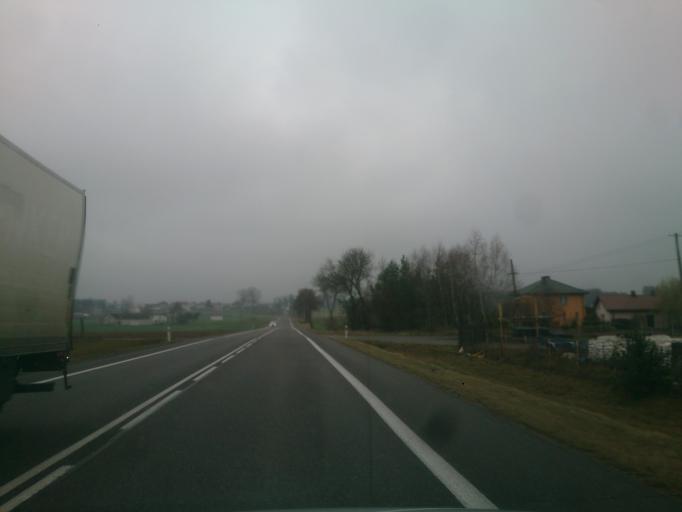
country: PL
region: Masovian Voivodeship
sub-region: Powiat plocki
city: Starozreby
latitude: 52.6527
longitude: 20.0859
